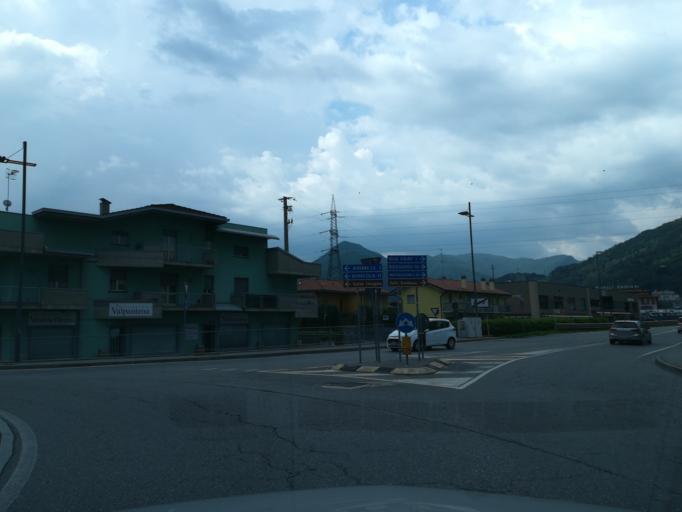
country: IT
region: Lombardy
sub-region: Provincia di Bergamo
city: Alme
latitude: 45.7422
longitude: 9.6106
